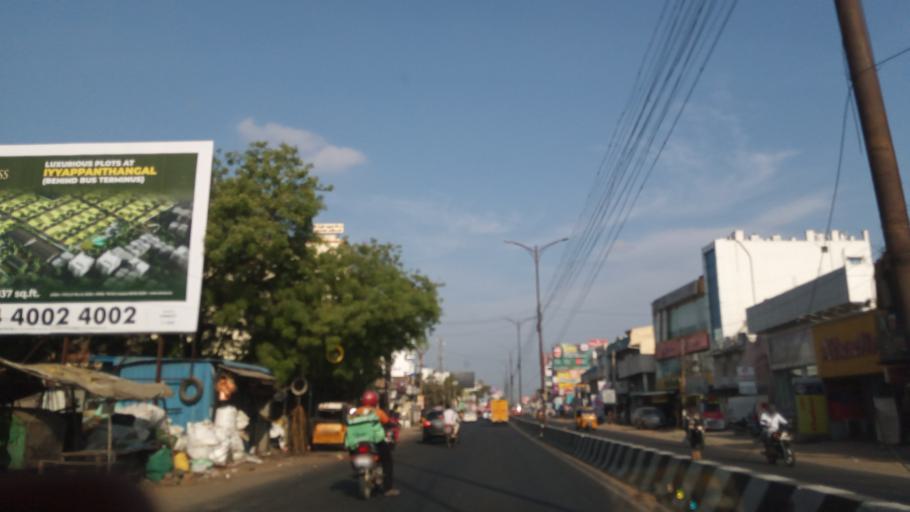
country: IN
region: Tamil Nadu
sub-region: Kancheepuram
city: Poonamalle
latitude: 13.0437
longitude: 80.1211
